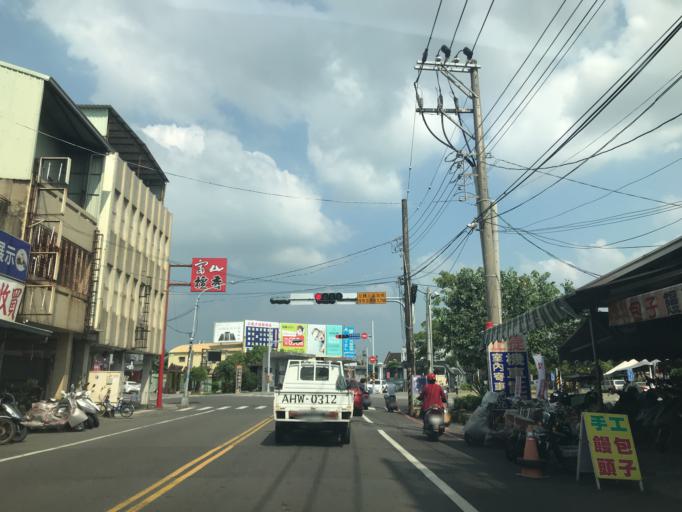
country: TW
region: Taiwan
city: Yujing
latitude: 23.1334
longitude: 120.3053
